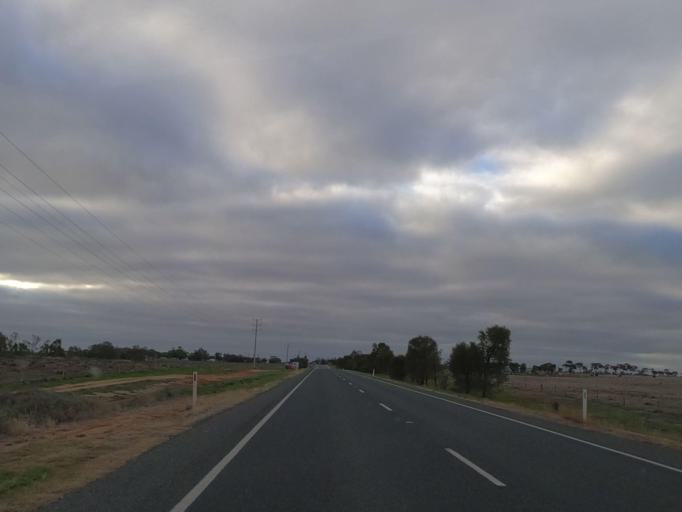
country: AU
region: Victoria
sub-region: Swan Hill
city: Swan Hill
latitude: -35.6182
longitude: 143.8034
